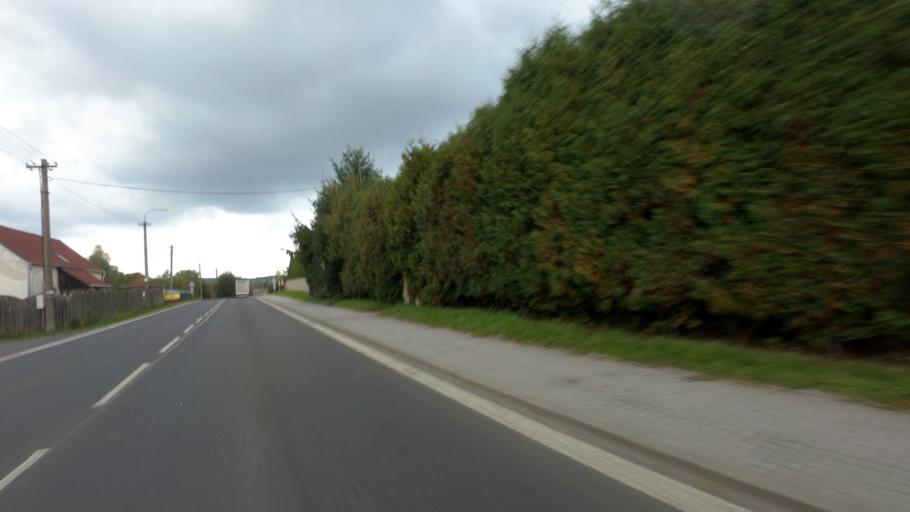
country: CZ
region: Ustecky
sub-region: Okres Decin
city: Rumburk
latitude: 50.9577
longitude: 14.5433
